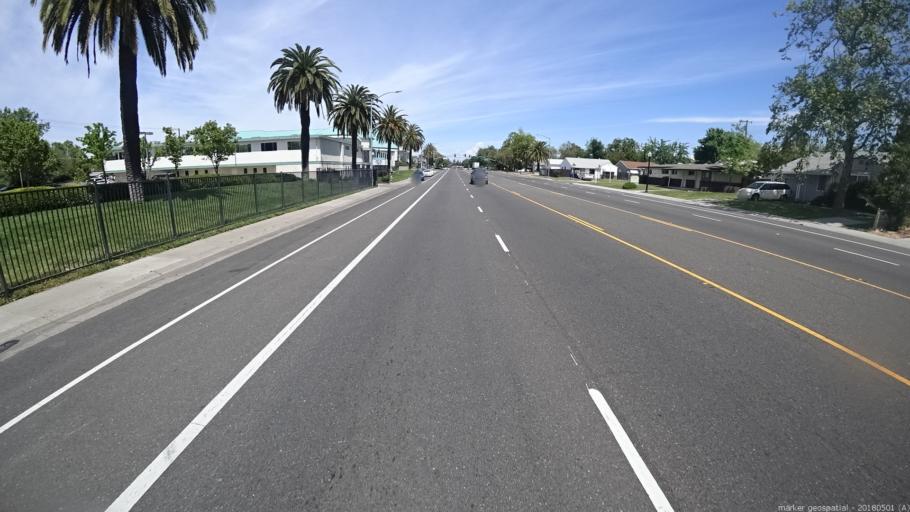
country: US
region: California
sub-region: Sacramento County
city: Sacramento
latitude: 38.6146
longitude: -121.4442
